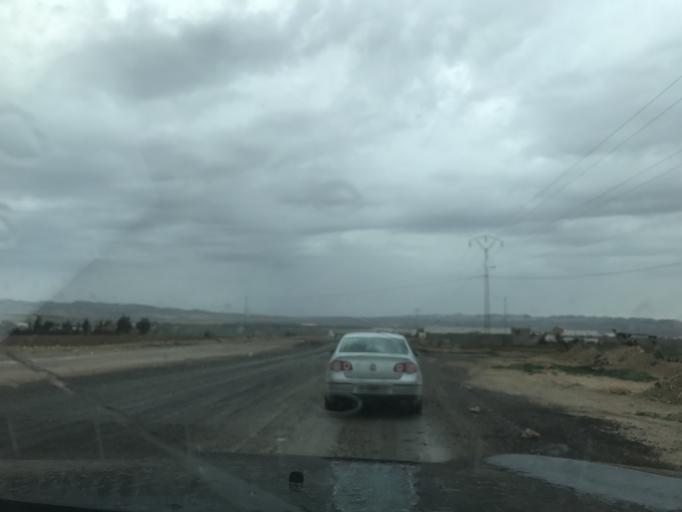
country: TN
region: Silyanah
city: Siliana
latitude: 36.0792
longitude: 9.4084
